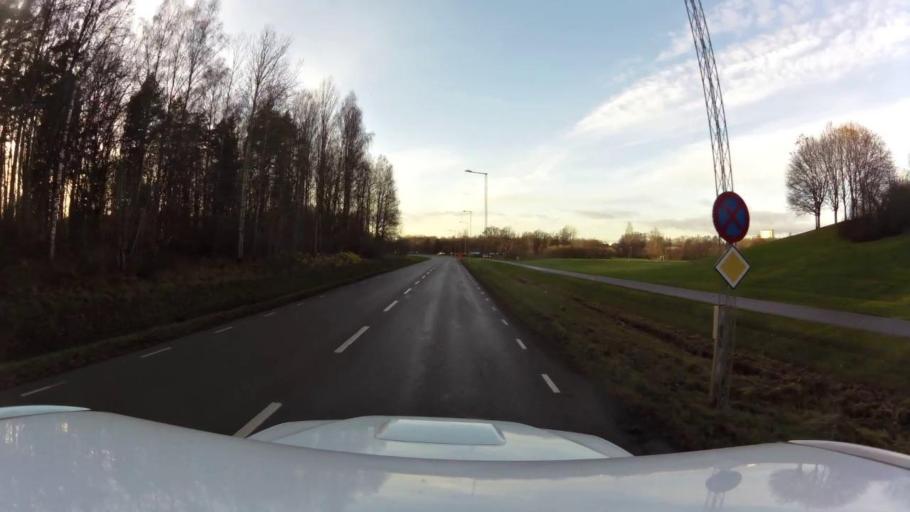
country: SE
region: OEstergoetland
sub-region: Linkopings Kommun
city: Linkoping
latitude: 58.3834
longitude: 15.6340
